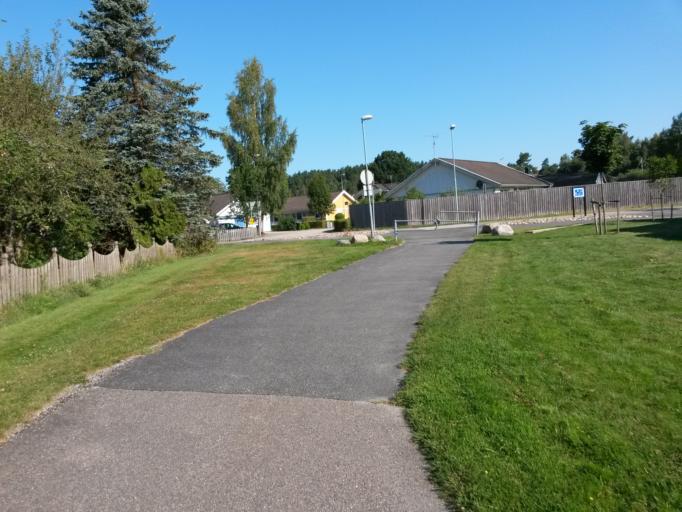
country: SE
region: Vaestra Goetaland
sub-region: Vargarda Kommun
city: Vargarda
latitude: 58.0429
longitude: 12.8155
